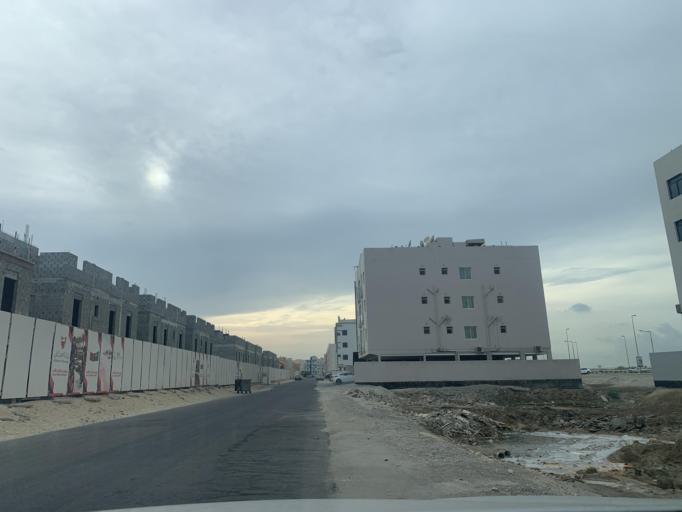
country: BH
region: Muharraq
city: Al Hadd
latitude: 26.2797
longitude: 50.6509
